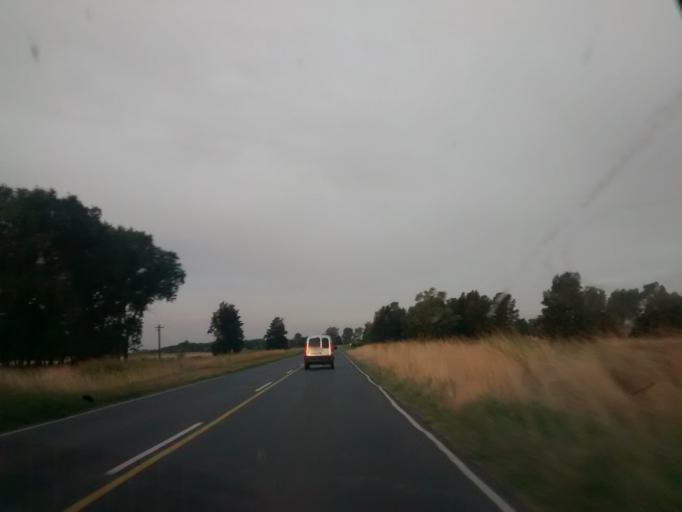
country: AR
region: Buenos Aires
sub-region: Partido de General Belgrano
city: General Belgrano
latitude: -35.7841
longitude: -58.5385
